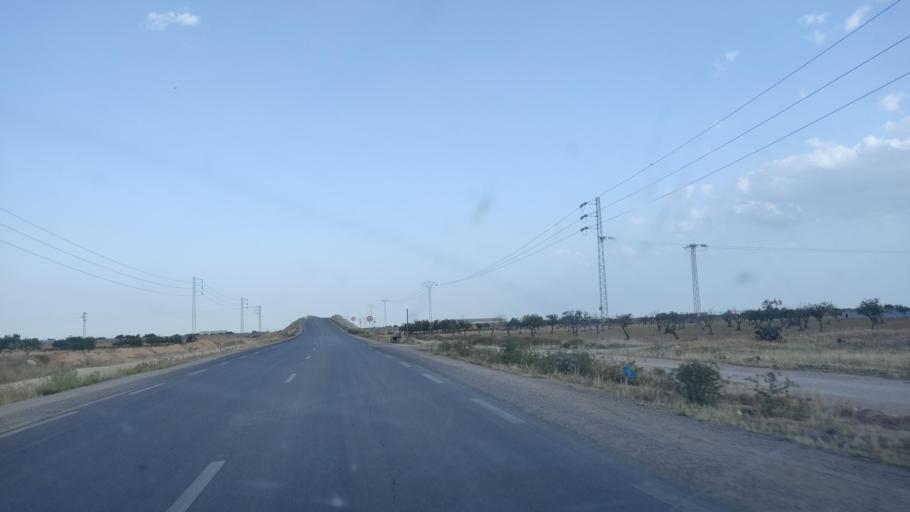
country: TN
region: Safaqis
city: Sfax
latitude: 34.8277
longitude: 10.6409
